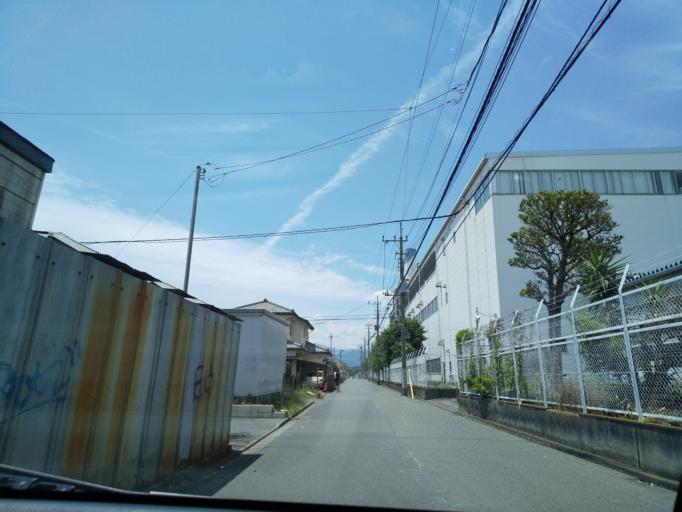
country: JP
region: Kanagawa
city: Zama
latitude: 35.5301
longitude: 139.3987
